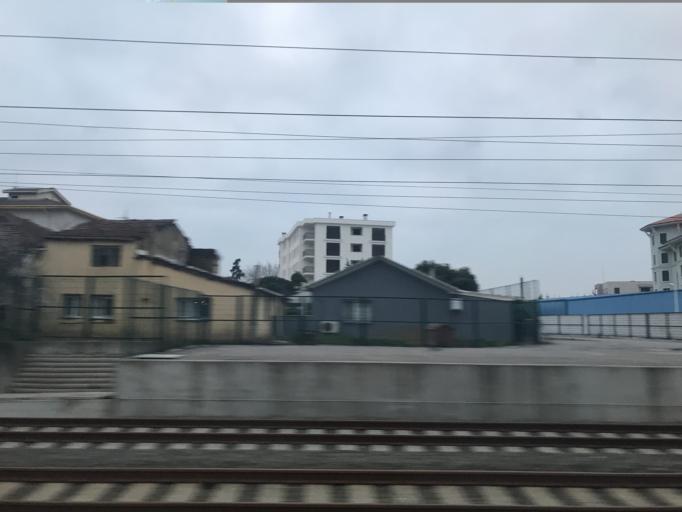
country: TR
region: Istanbul
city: Icmeler
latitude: 40.8315
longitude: 29.3199
